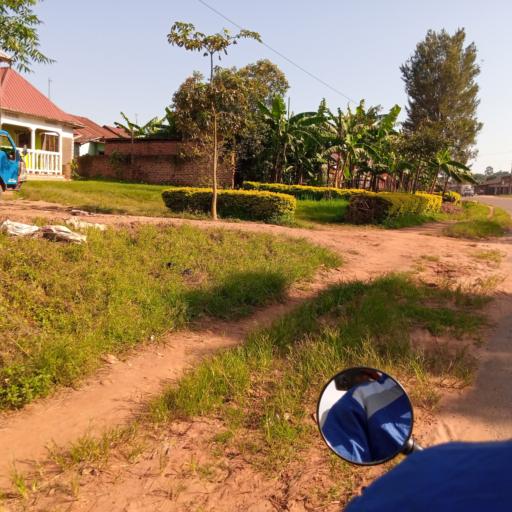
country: UG
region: Central Region
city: Masaka
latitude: -0.4489
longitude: 31.6685
